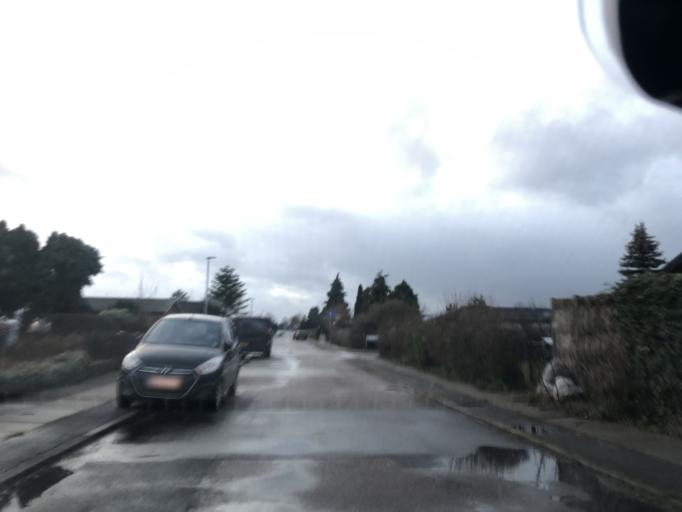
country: DK
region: Capital Region
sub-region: Tarnby Kommune
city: Tarnby
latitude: 55.6126
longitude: 12.6047
